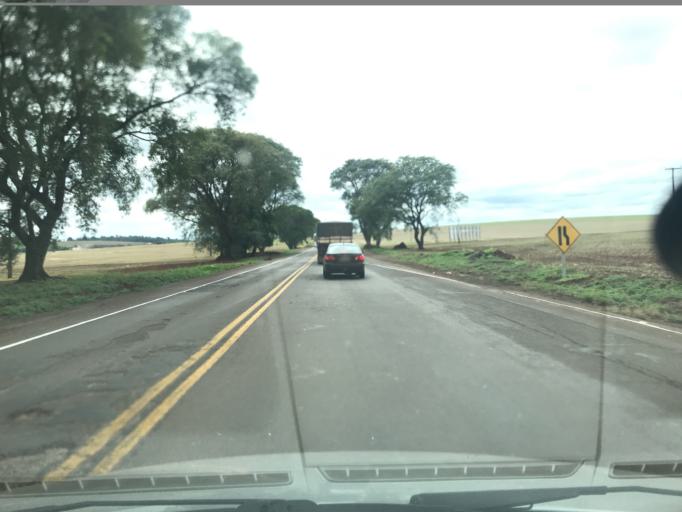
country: BR
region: Parana
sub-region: Terra Boa
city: Terra Boa
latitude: -23.6095
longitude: -52.4208
